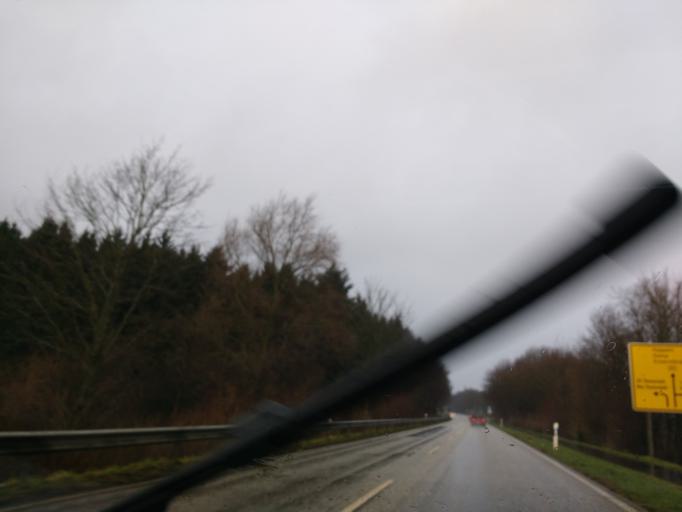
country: DE
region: Schleswig-Holstein
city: Borgstedt
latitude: 54.3558
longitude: 9.7039
